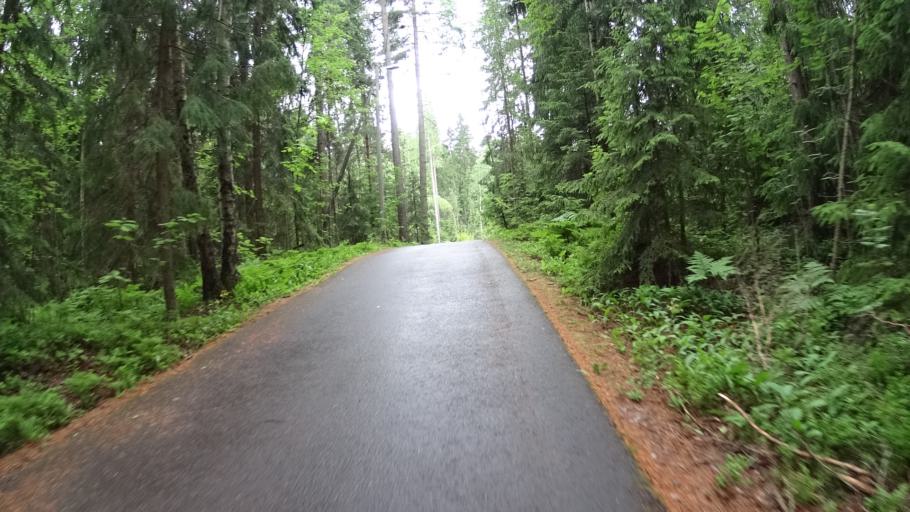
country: FI
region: Uusimaa
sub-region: Helsinki
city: Helsinki
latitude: 60.2596
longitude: 24.9024
